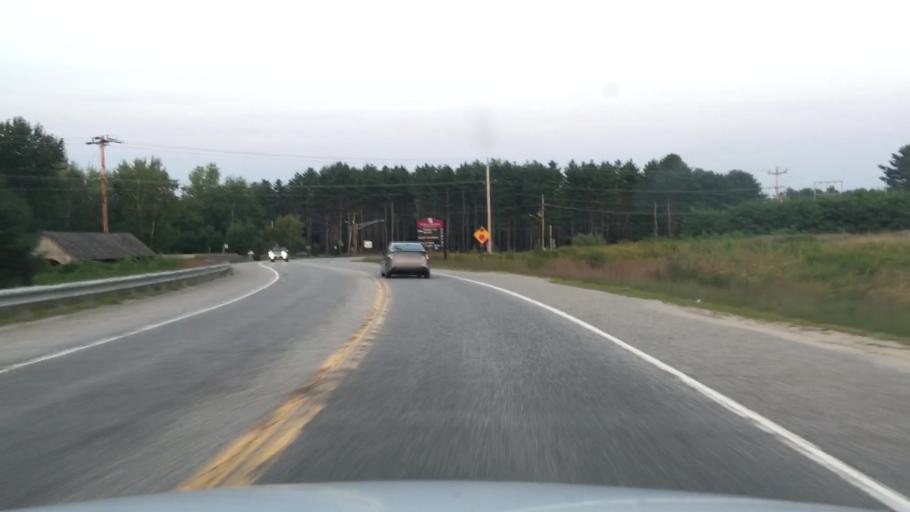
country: US
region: Maine
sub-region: Oxford County
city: Bethel
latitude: 44.4132
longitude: -70.7897
